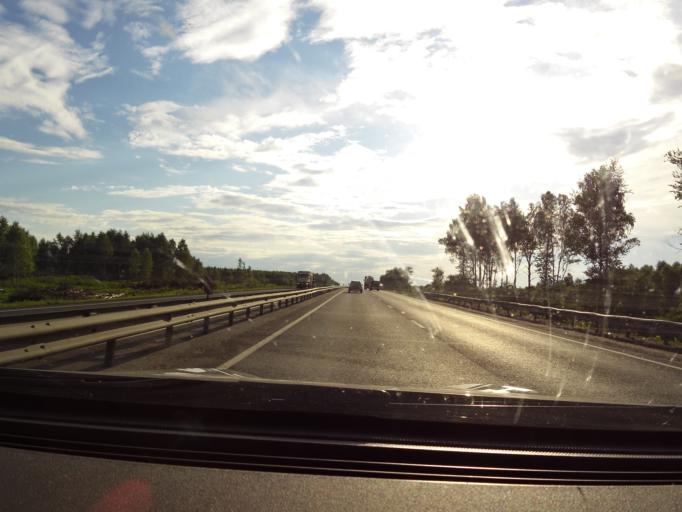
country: RU
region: Vladimir
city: Melekhovo
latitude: 56.2044
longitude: 41.1593
